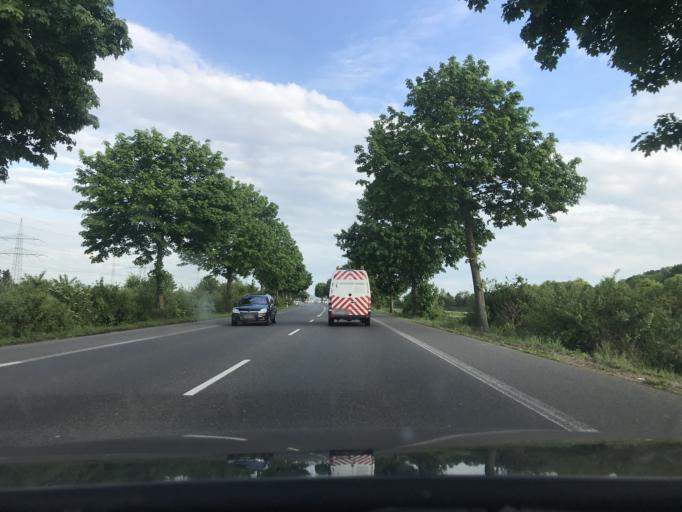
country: DE
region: North Rhine-Westphalia
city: Bornheim
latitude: 50.7710
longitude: 7.0015
